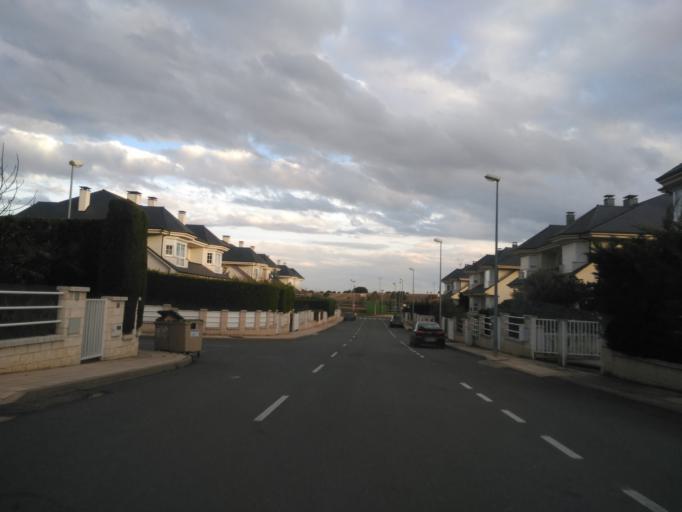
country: ES
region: Castille and Leon
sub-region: Provincia de Salamanca
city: Santa Marta de Tormes
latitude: 40.9289
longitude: -5.6264
